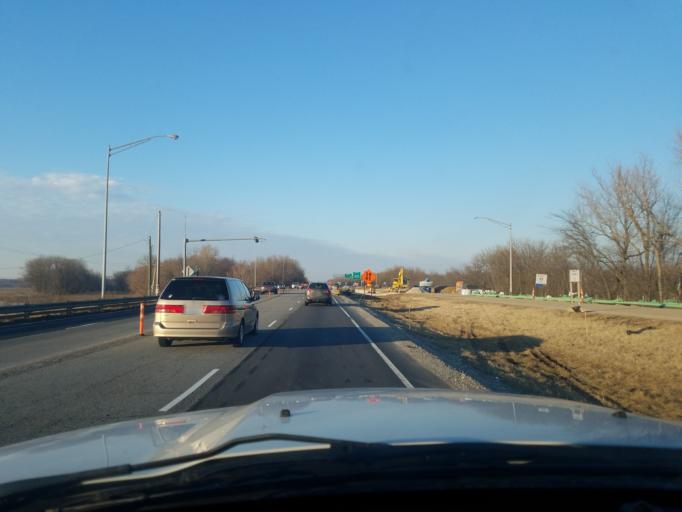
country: US
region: Indiana
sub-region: Vanderburgh County
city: Evansville
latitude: 37.9289
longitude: -87.5482
